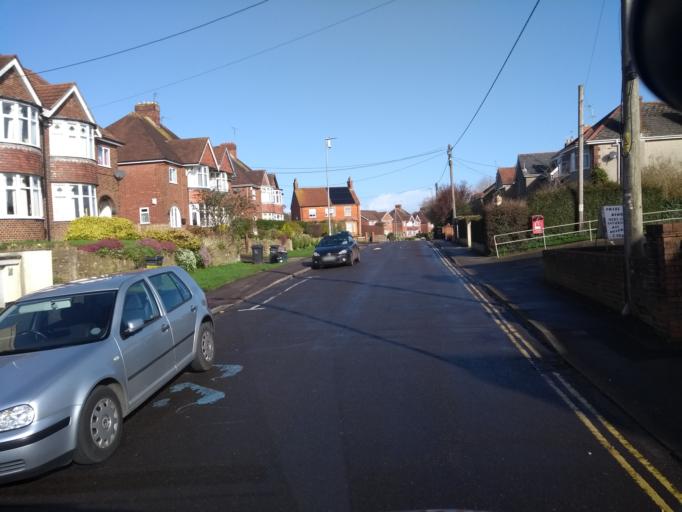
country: GB
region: England
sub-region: Somerset
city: Yeovil
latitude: 50.9498
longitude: -2.6219
